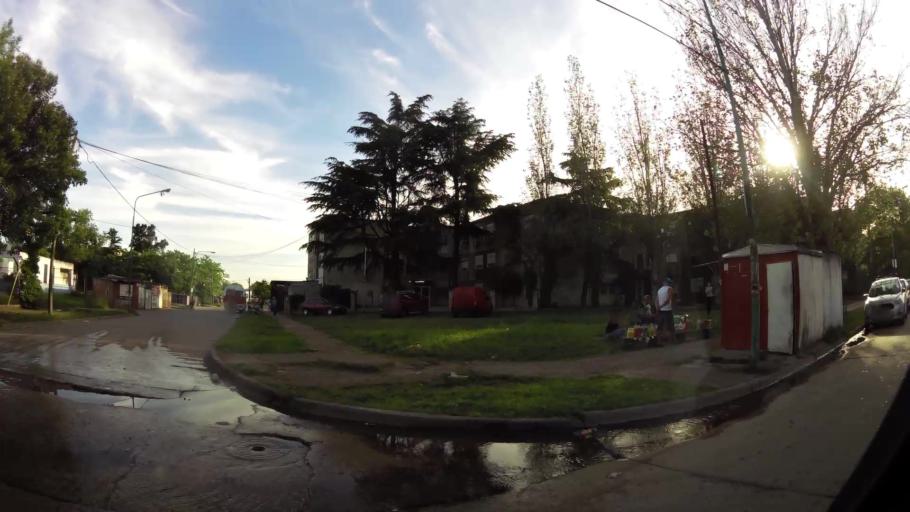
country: AR
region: Buenos Aires
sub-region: Partido de Almirante Brown
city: Adrogue
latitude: -34.8192
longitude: -58.3414
